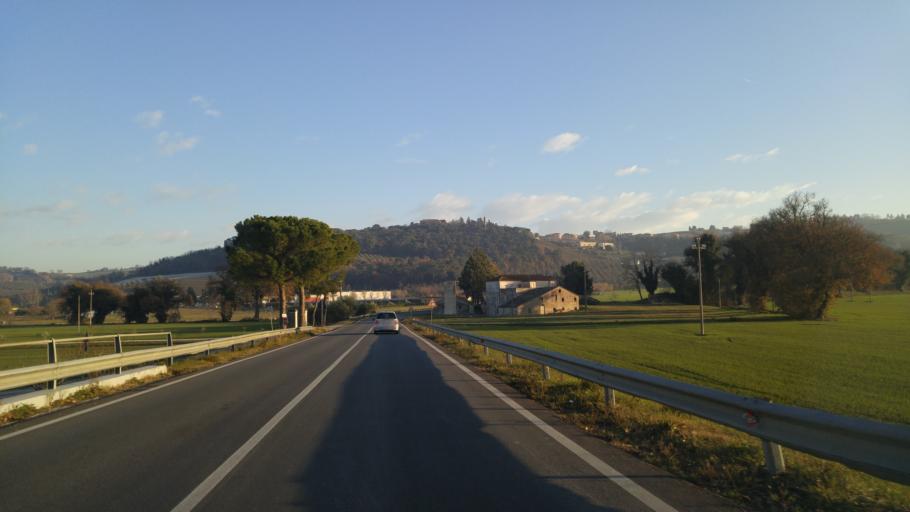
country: IT
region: The Marches
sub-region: Provincia di Ancona
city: Monterado
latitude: 43.7055
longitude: 13.0819
